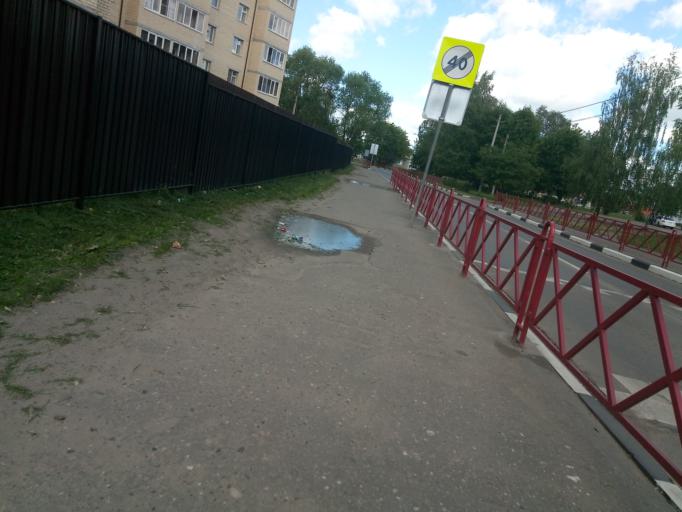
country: RU
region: Jaroslavl
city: Yaroslavl
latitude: 57.6575
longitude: 39.9564
